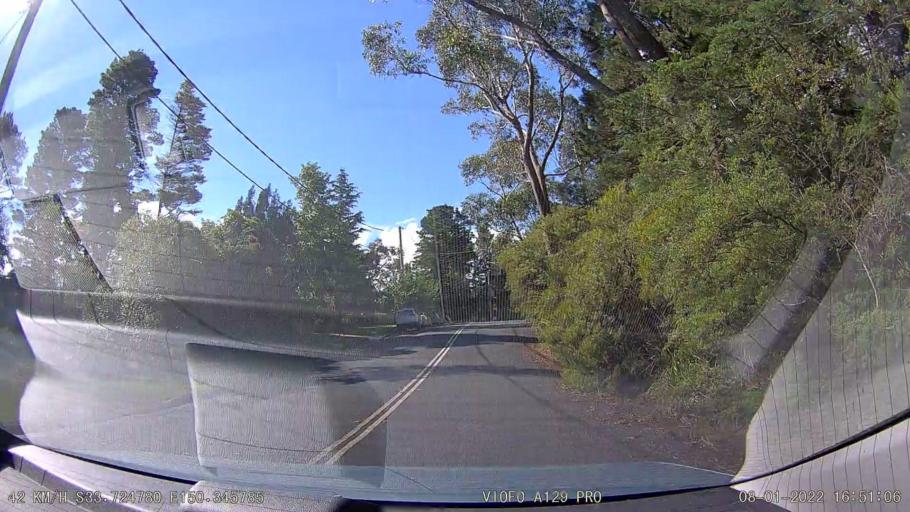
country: AU
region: New South Wales
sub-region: Blue Mountains Municipality
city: Leura
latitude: -33.7249
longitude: 150.3458
